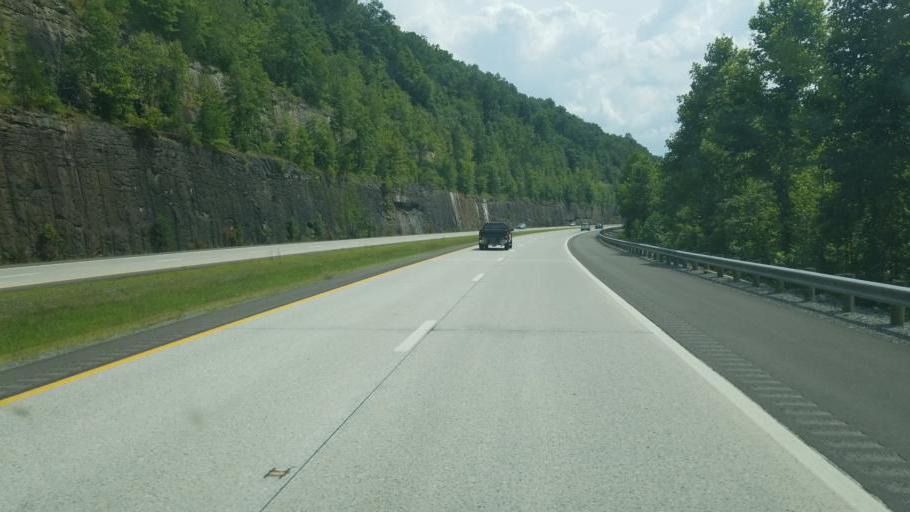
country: US
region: West Virginia
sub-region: Kanawha County
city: Alum Creek
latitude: 38.1935
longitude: -81.8456
